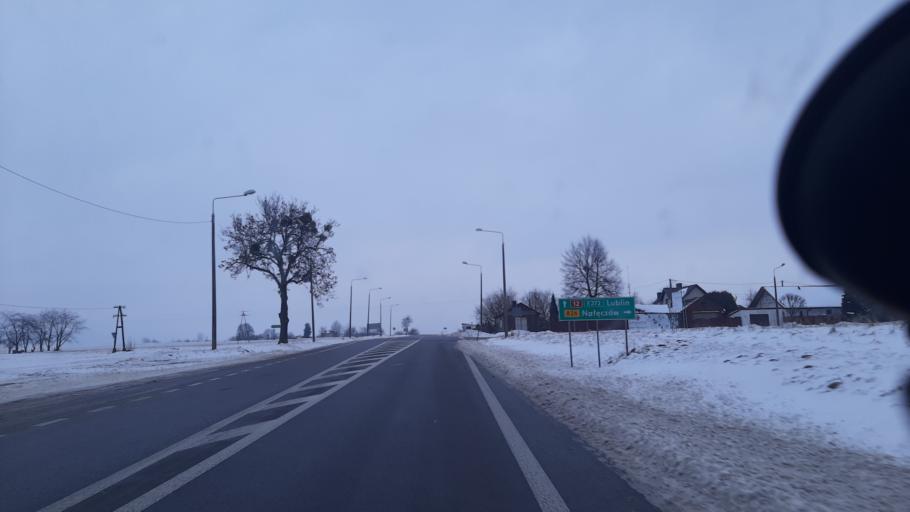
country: PL
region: Lublin Voivodeship
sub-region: Powiat pulawski
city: Markuszow
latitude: 51.3696
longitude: 22.2801
